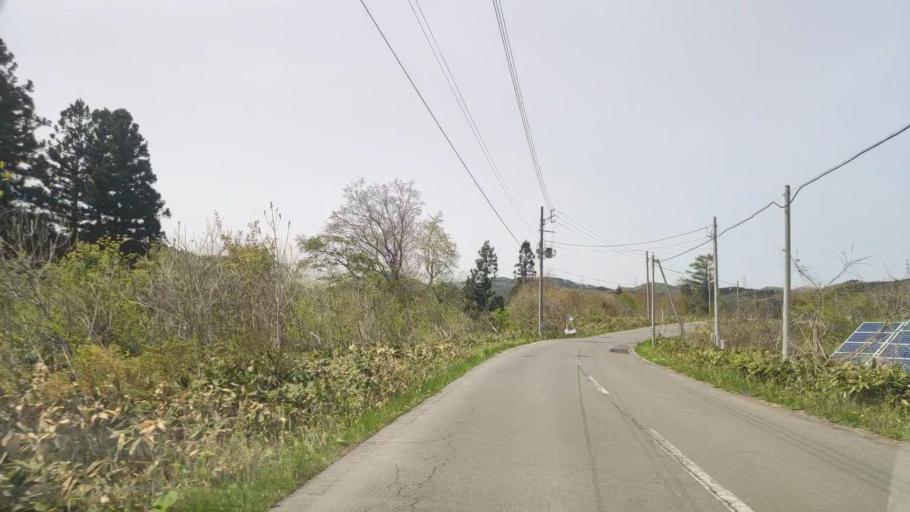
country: JP
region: Aomori
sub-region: Misawa Shi
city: Inuotose
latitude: 40.7846
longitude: 141.1139
